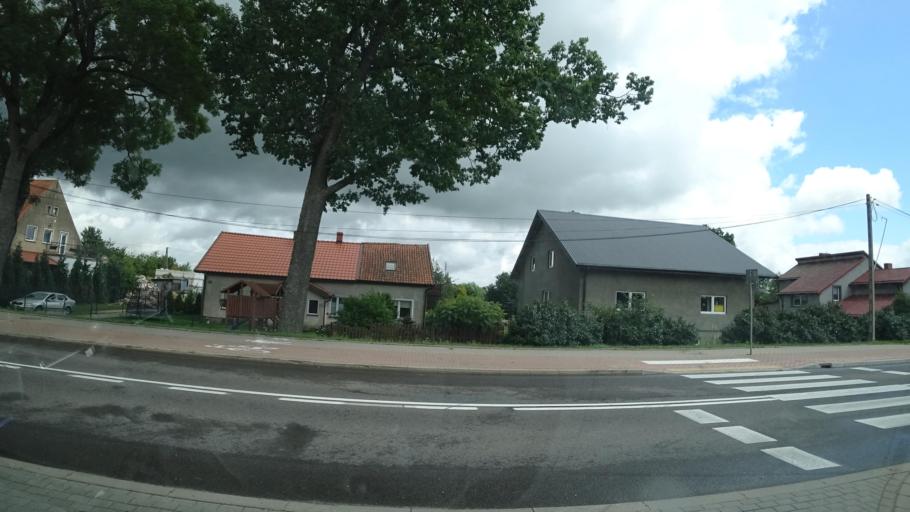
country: PL
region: Warmian-Masurian Voivodeship
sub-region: Powiat olecki
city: Kowale Oleckie
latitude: 54.1612
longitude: 22.4171
